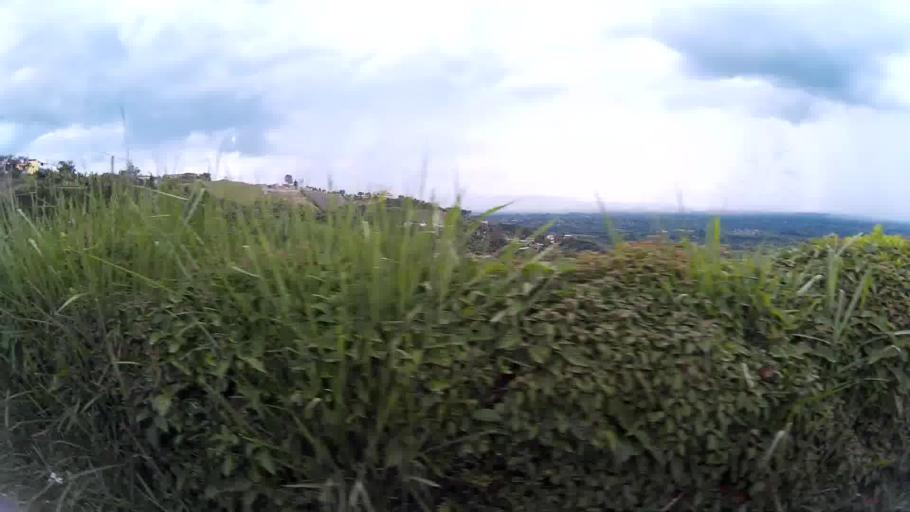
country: CO
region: Valle del Cauca
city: Ulloa
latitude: 4.7532
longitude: -75.7138
